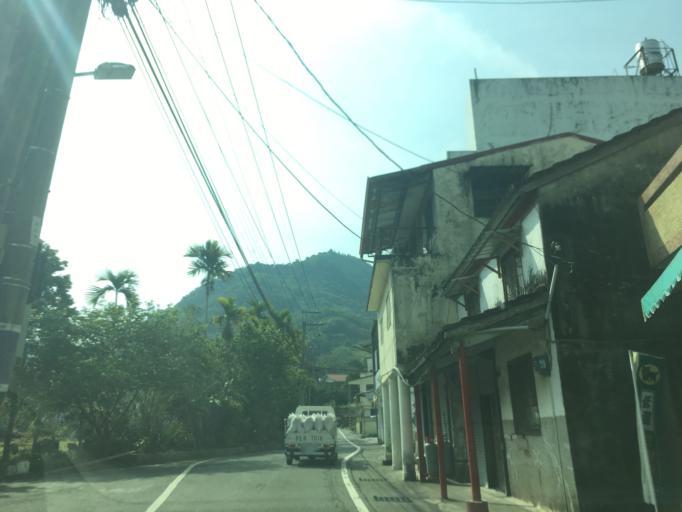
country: TW
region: Taiwan
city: Fengyuan
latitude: 24.1587
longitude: 120.8267
